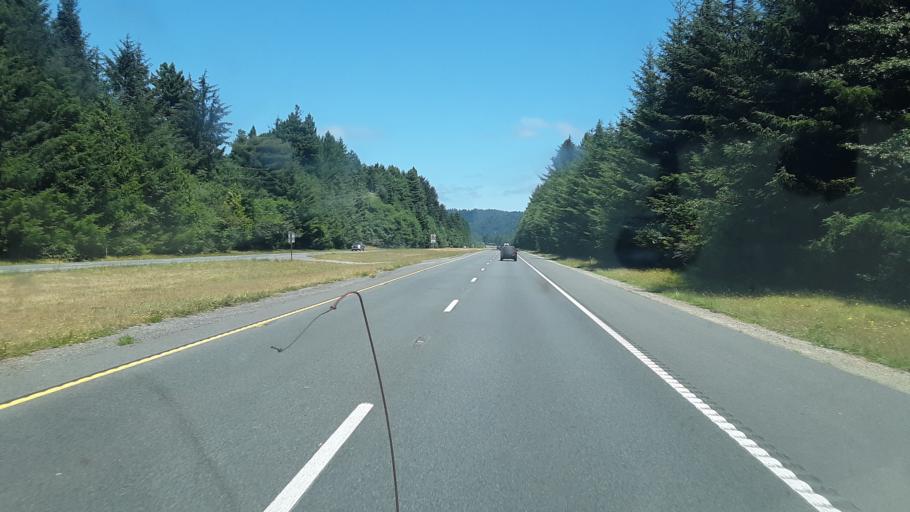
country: US
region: California
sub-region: Del Norte County
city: Bertsch-Oceanview
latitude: 41.7856
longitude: -124.1709
